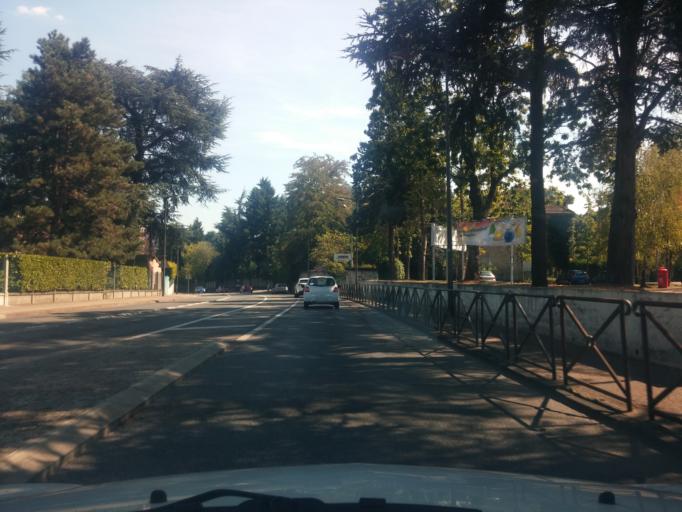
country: FR
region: Rhone-Alpes
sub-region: Departement du Rhone
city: Francheville
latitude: 45.7378
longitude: 4.7737
